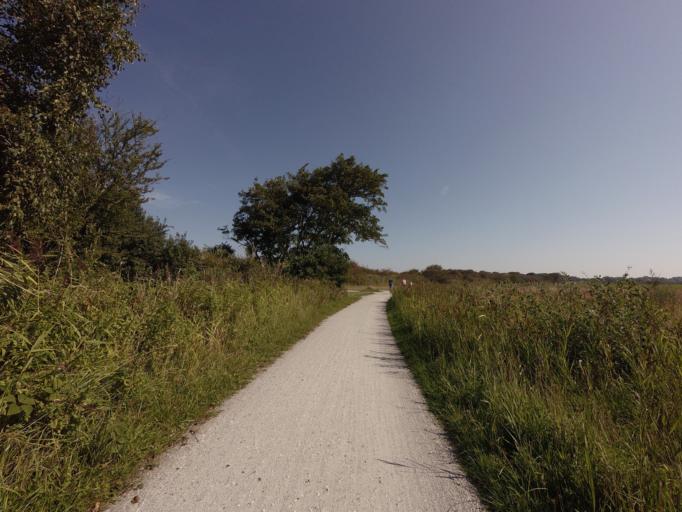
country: NL
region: Friesland
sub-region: Gemeente Schiermonnikoog
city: Schiermonnikoog
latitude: 53.4769
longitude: 6.1387
